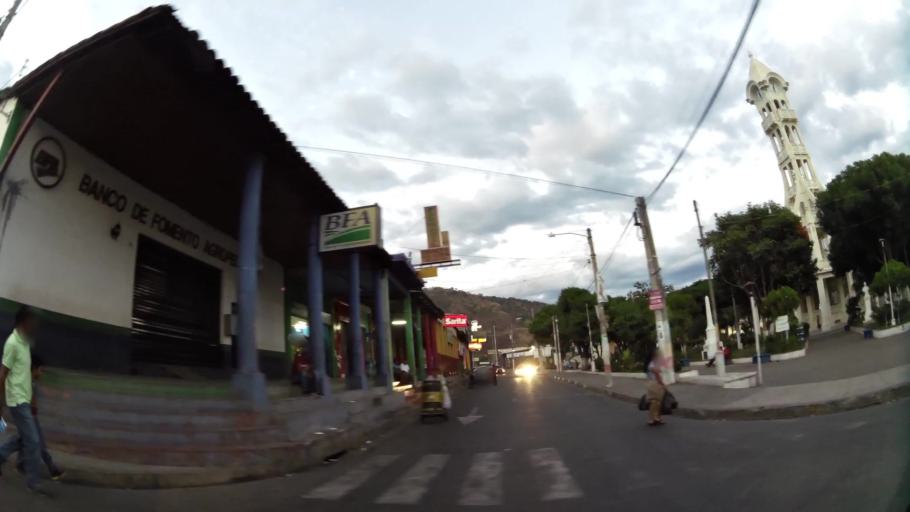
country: SV
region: San Vicente
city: San Vicente
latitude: 13.6449
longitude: -88.7846
